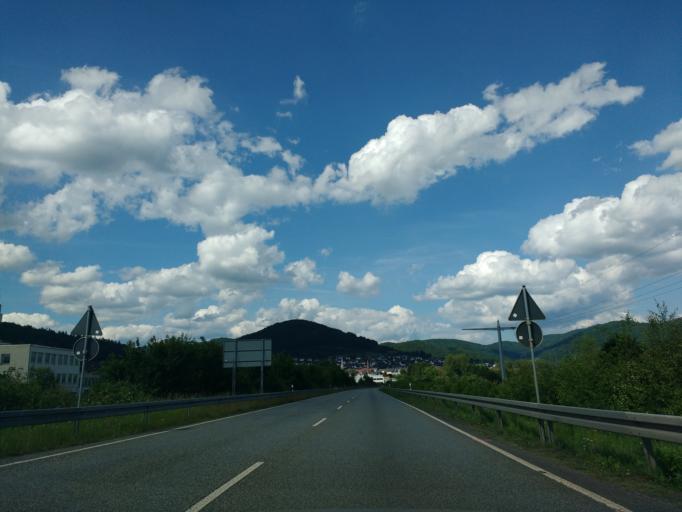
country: DE
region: Hesse
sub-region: Regierungsbezirk Giessen
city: Breidenbach
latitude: 50.9213
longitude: 8.4692
